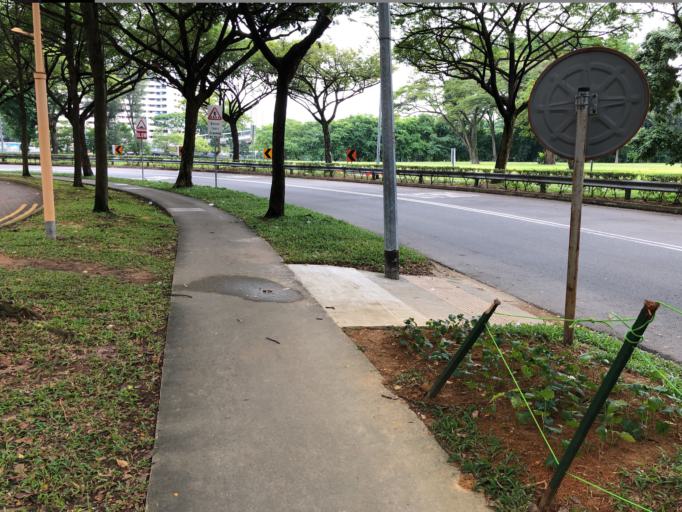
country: SG
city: Singapore
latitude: 1.3282
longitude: 103.8604
